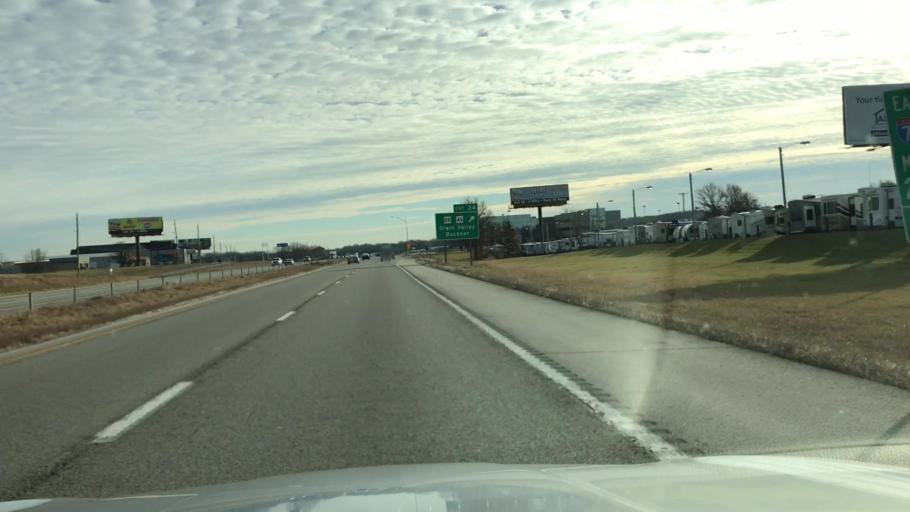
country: US
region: Missouri
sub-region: Jackson County
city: Grain Valley
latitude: 39.0222
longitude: -94.2055
